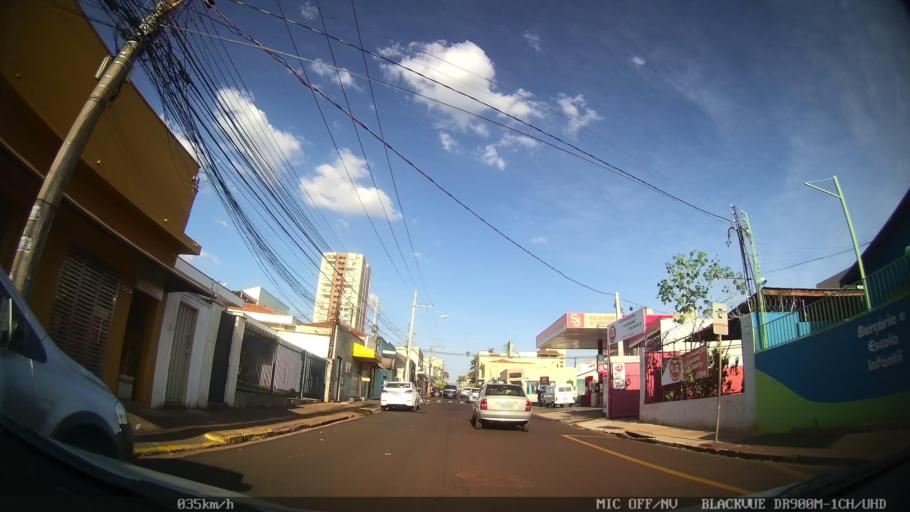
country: BR
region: Sao Paulo
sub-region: Ribeirao Preto
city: Ribeirao Preto
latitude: -21.1820
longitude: -47.7941
